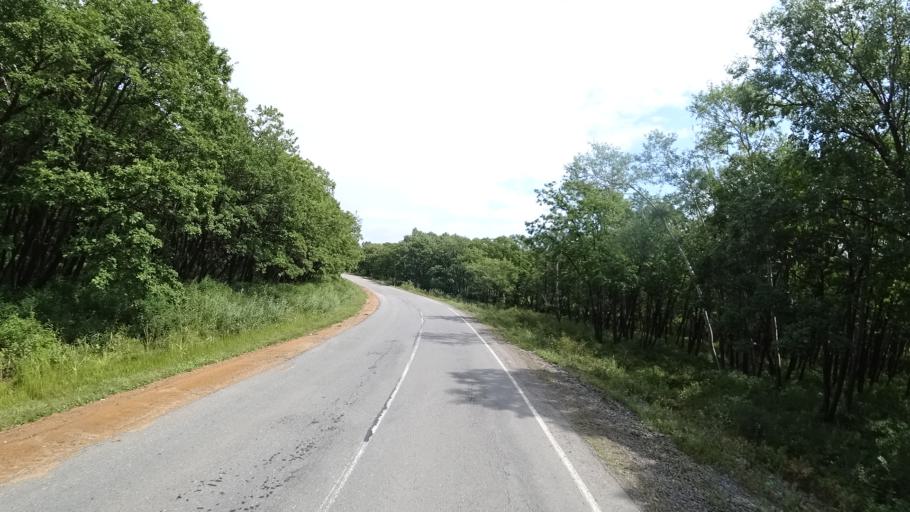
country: RU
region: Primorskiy
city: Lyalichi
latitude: 44.1398
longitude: 132.4124
